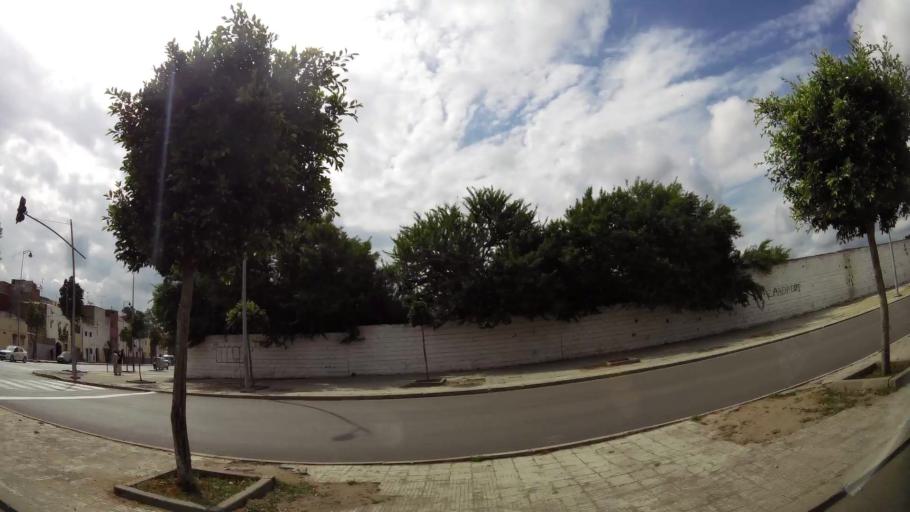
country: MA
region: Gharb-Chrarda-Beni Hssen
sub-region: Kenitra Province
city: Kenitra
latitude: 34.2590
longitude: -6.5654
